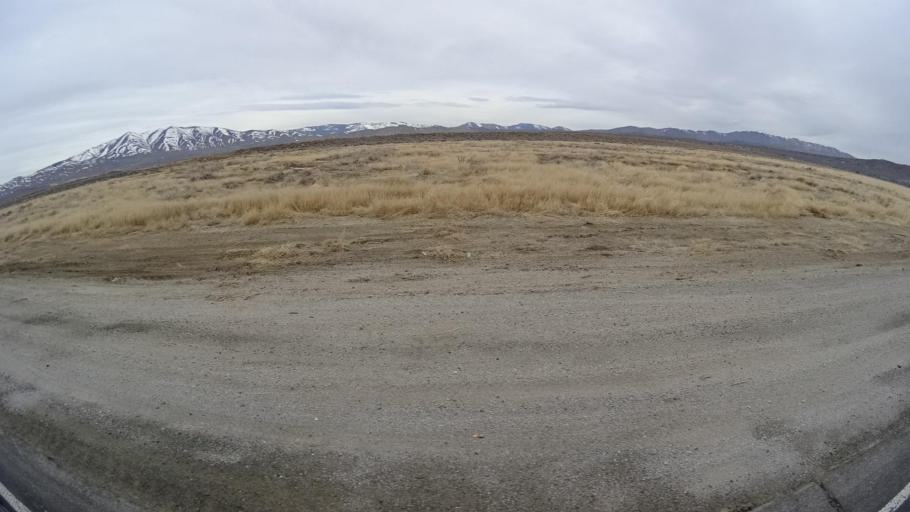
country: US
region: Nevada
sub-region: Washoe County
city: Lemmon Valley
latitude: 39.6596
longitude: -119.8283
